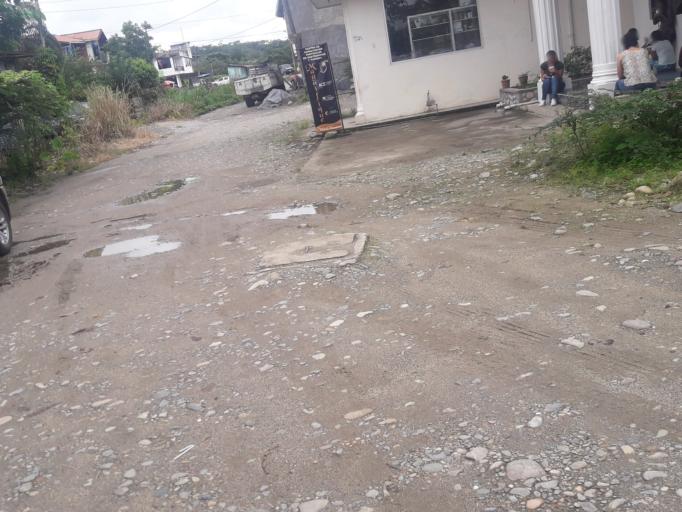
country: EC
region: Napo
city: Tena
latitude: -0.9984
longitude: -77.8109
